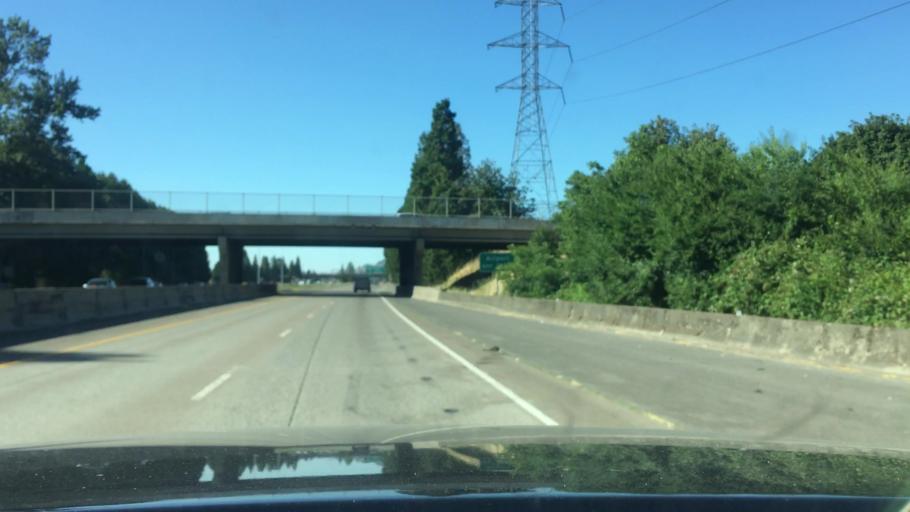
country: US
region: Oregon
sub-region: Lane County
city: Springfield
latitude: 44.0550
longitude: -123.0500
